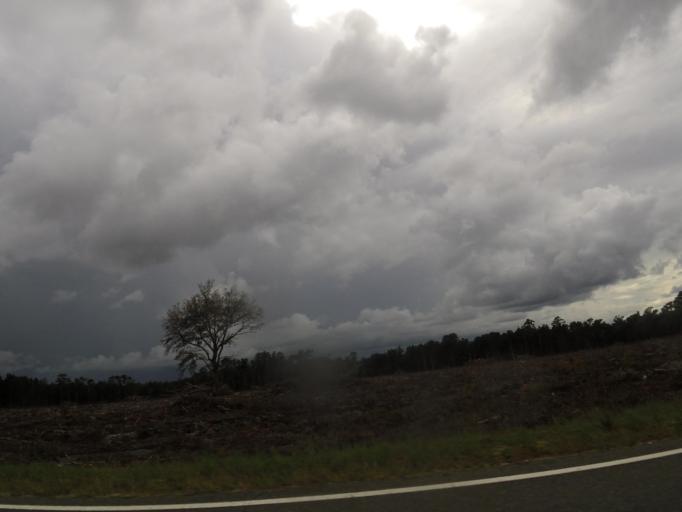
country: US
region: Florida
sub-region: Baker County
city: Macclenny
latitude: 30.5146
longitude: -82.2231
